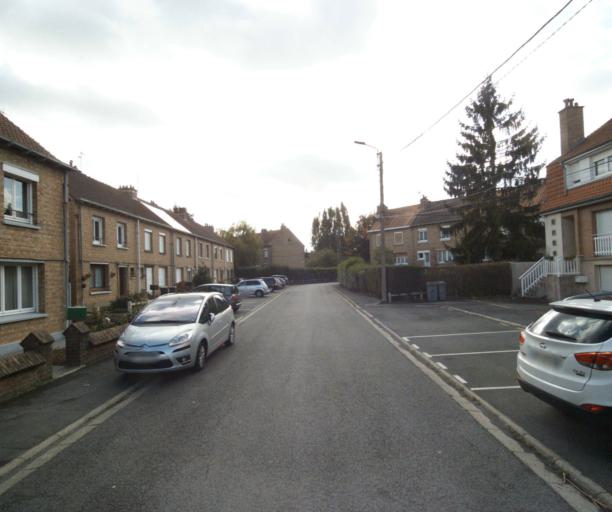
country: FR
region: Nord-Pas-de-Calais
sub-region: Departement du Nord
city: Armentieres
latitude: 50.6745
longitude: 2.8958
